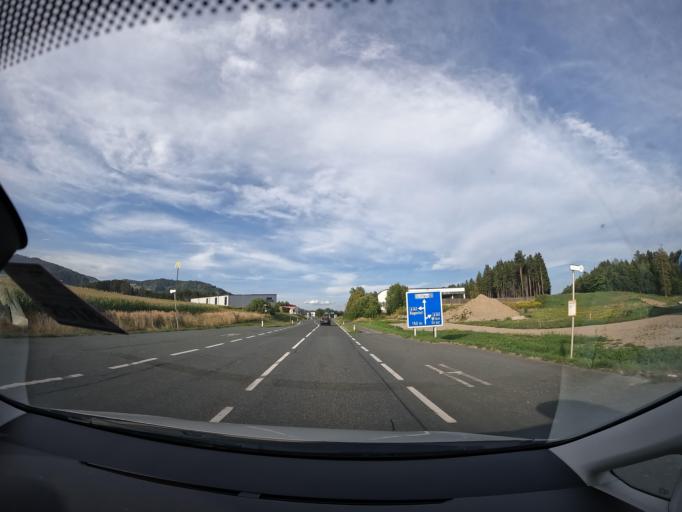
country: AT
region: Carinthia
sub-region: Politischer Bezirk Volkermarkt
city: Voelkermarkt
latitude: 46.6802
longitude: 14.6760
